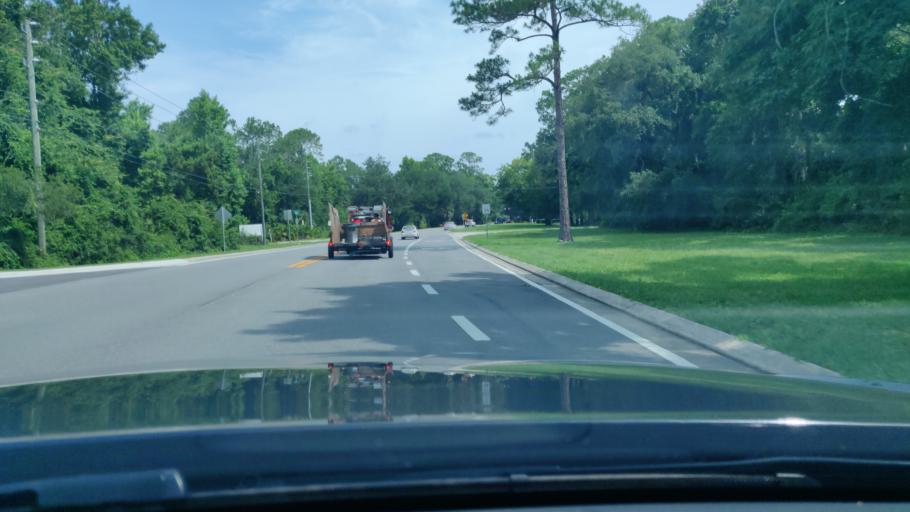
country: US
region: Florida
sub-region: Flagler County
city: Palm Coast
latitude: 29.5542
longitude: -81.1967
